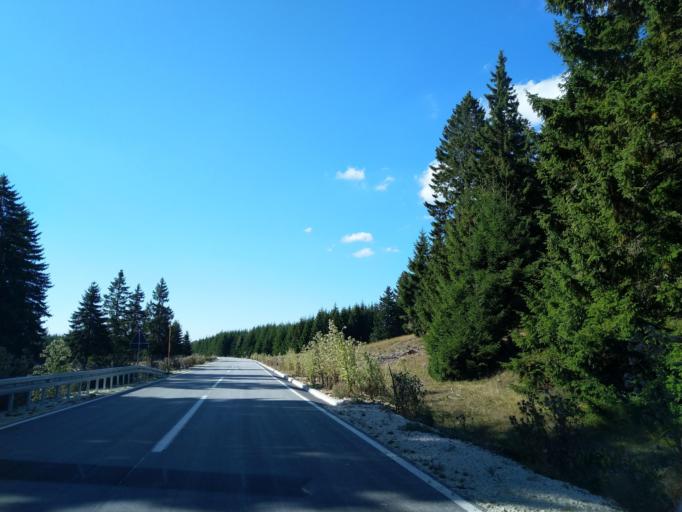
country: RS
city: Sokolovica
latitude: 43.2885
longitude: 20.3181
